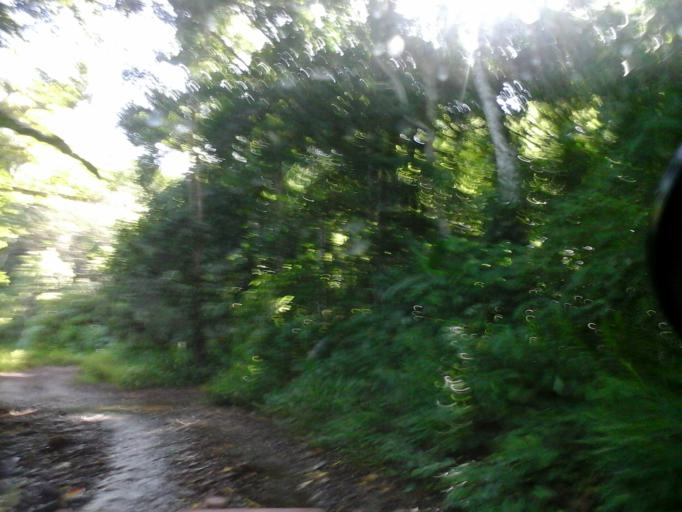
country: CO
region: Cesar
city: San Diego
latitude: 10.2617
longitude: -73.1075
